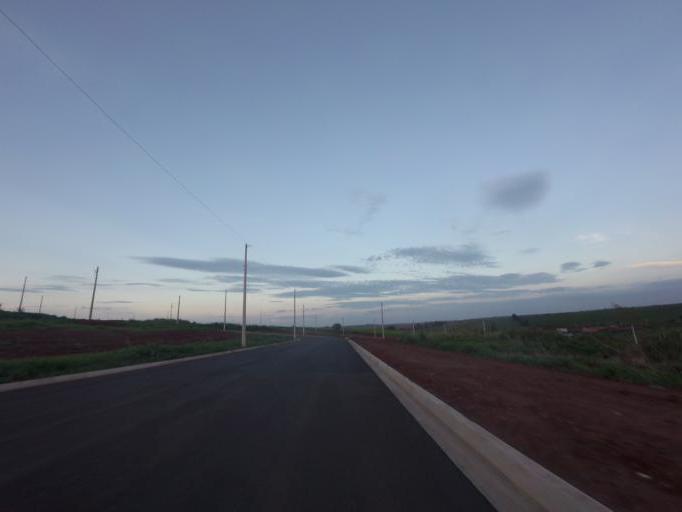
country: BR
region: Sao Paulo
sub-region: Piracicaba
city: Piracicaba
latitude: -22.7625
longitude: -47.5810
